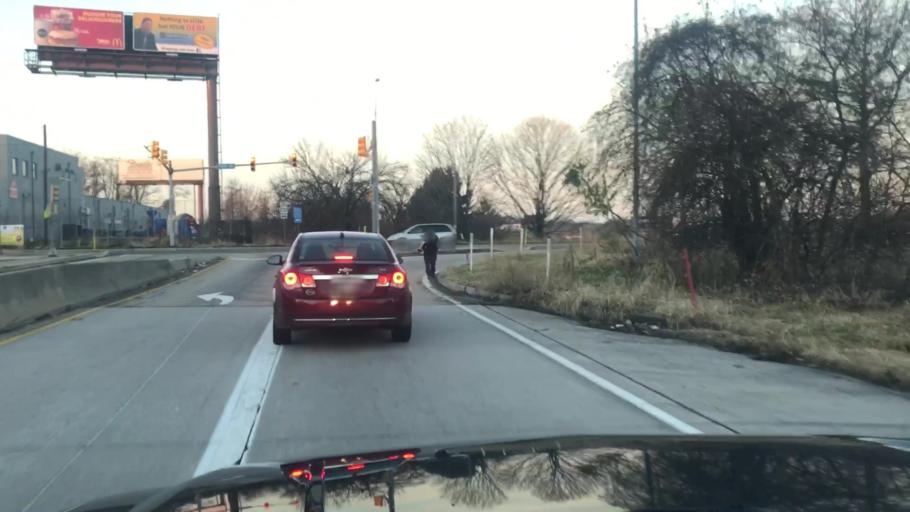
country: US
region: Pennsylvania
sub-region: Dauphin County
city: Penbrook
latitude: 40.2537
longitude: -76.8637
